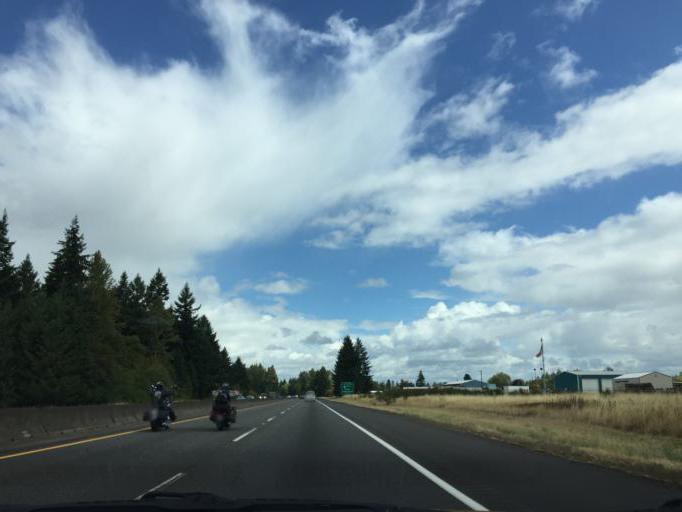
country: US
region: Washington
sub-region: Lewis County
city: Winlock
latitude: 46.4007
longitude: -122.8974
